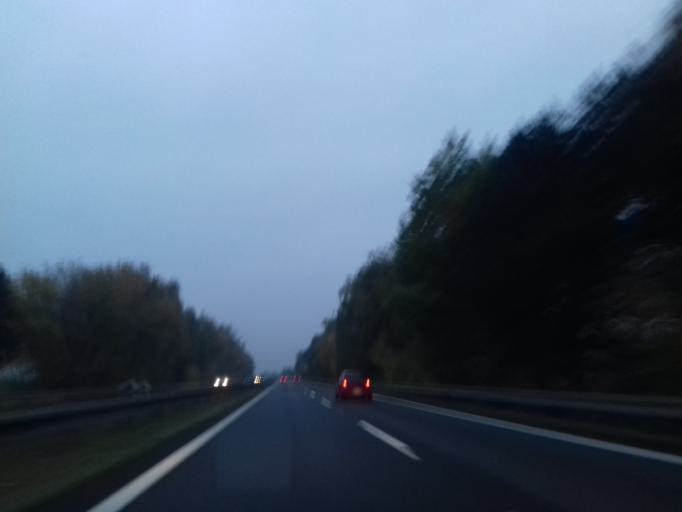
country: CZ
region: Olomoucky
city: Naklo
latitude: 49.6671
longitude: 17.0955
